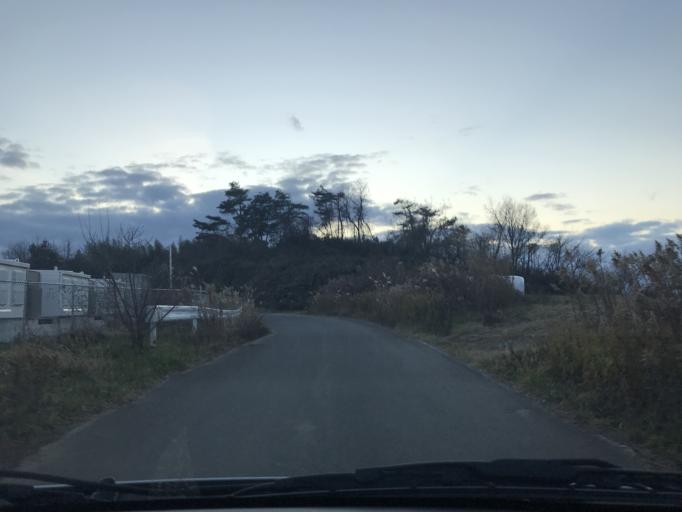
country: JP
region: Iwate
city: Ichinoseki
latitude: 38.8331
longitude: 141.0953
